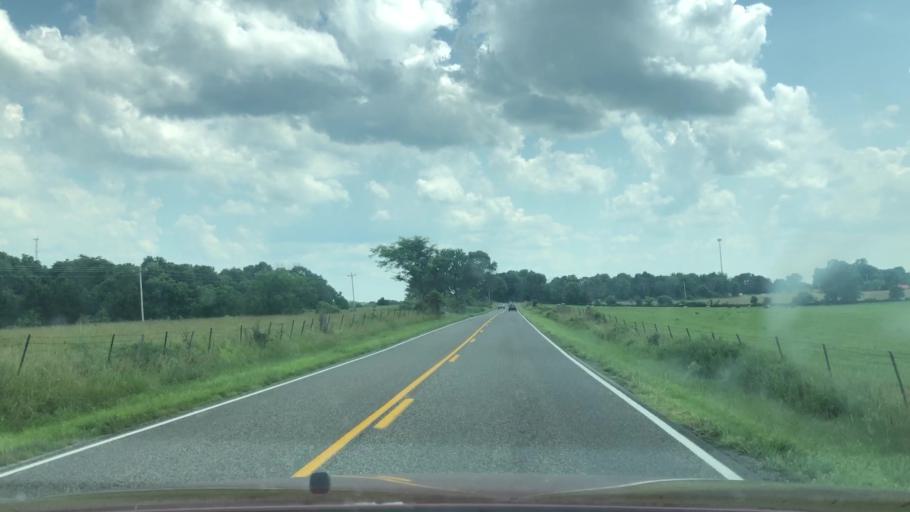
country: US
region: Missouri
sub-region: Christian County
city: Ozark
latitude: 36.9394
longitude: -93.2536
